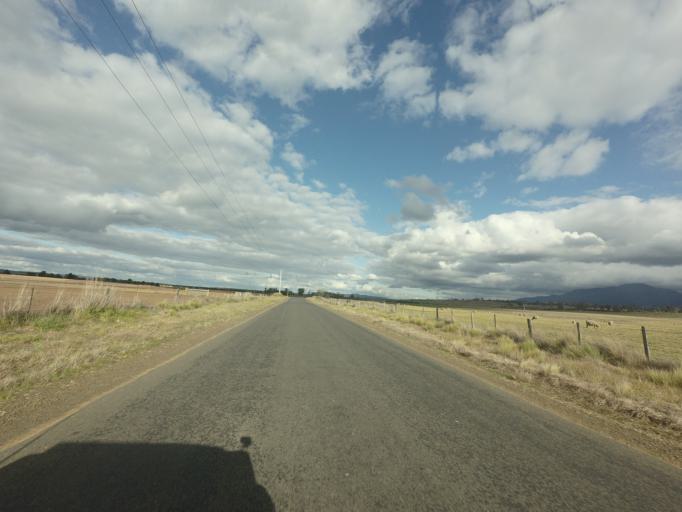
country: AU
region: Tasmania
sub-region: Northern Midlands
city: Longford
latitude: -41.8105
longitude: 147.1871
